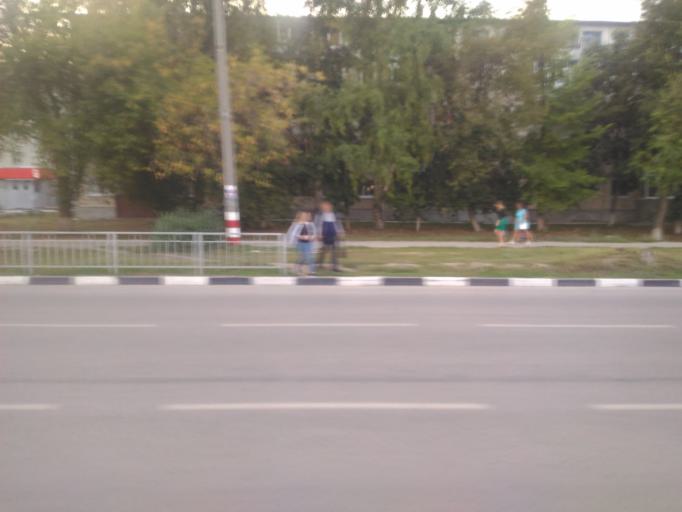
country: RU
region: Ulyanovsk
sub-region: Ulyanovskiy Rayon
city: Ulyanovsk
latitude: 54.2730
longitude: 48.2881
